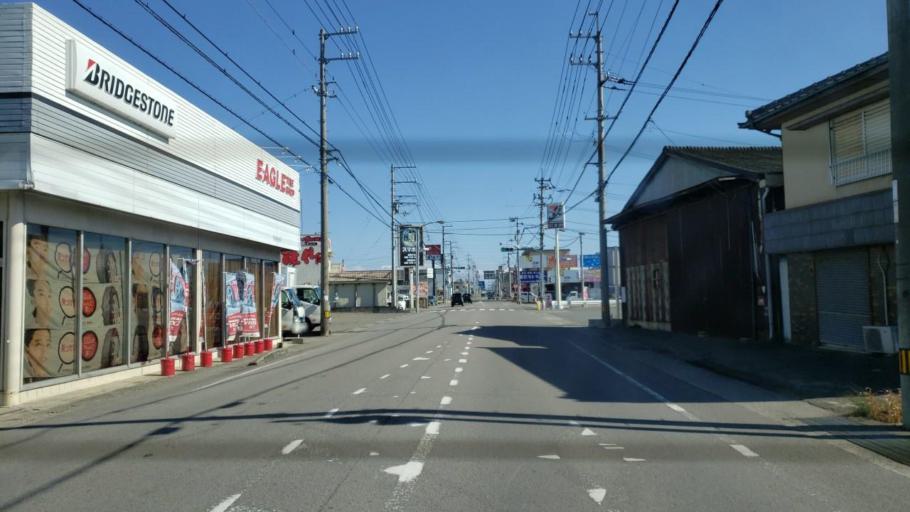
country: JP
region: Tokushima
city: Tokushima-shi
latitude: 34.1333
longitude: 134.5140
